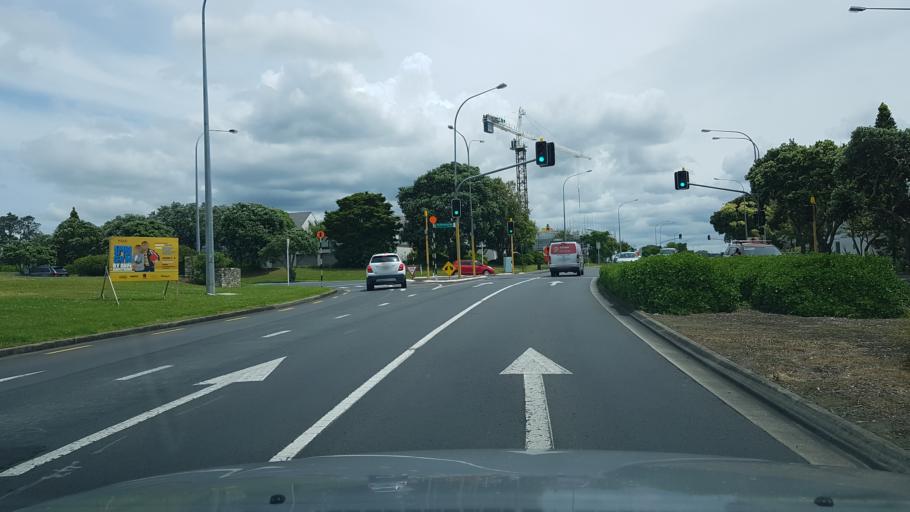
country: NZ
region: Auckland
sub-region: Auckland
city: North Shore
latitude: -36.7997
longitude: 174.7578
